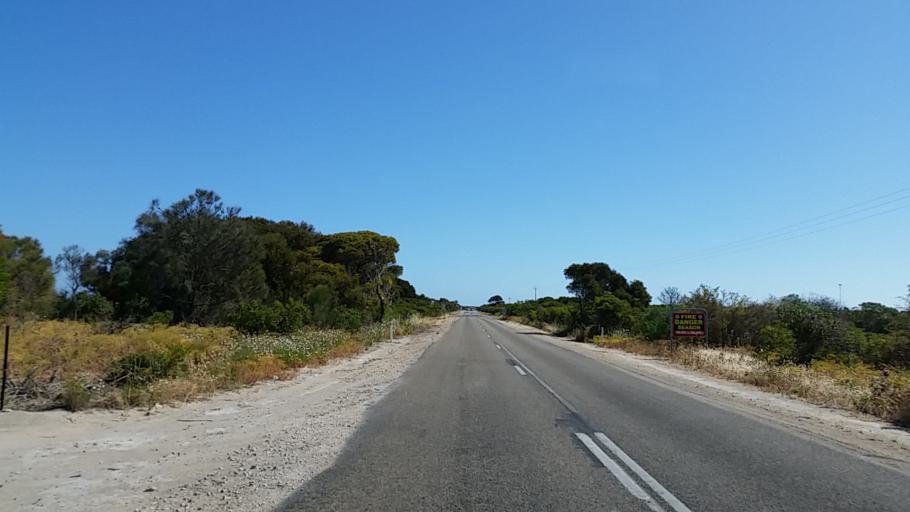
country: AU
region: South Australia
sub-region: Yorke Peninsula
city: Honiton
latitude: -35.2301
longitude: 136.9843
